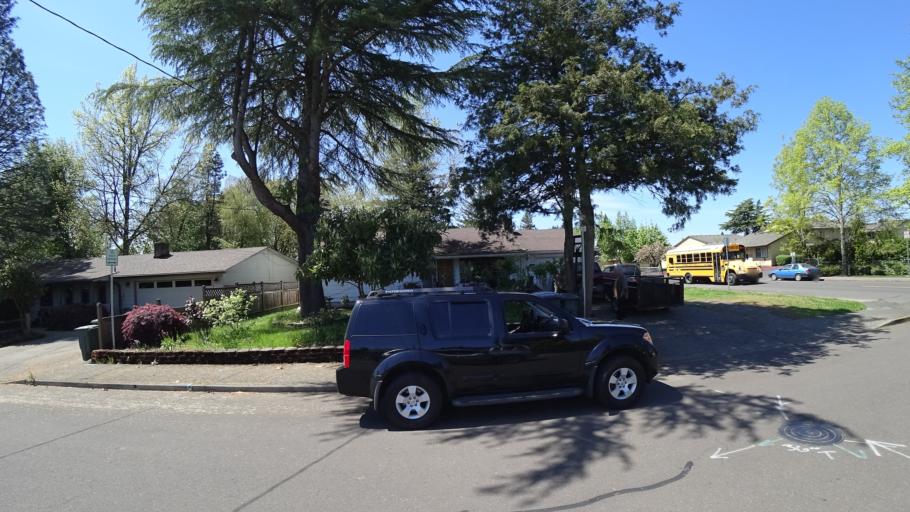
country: US
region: Oregon
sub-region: Washington County
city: Hillsboro
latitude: 45.5147
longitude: -122.9665
